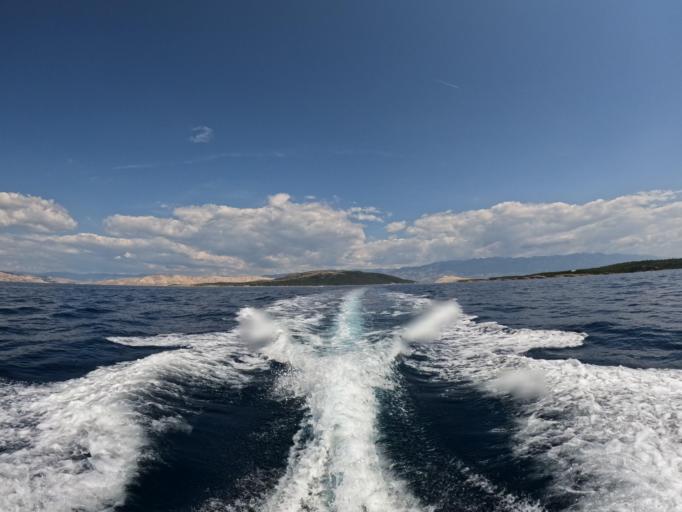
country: HR
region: Primorsko-Goranska
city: Lopar
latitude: 44.8561
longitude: 14.7084
